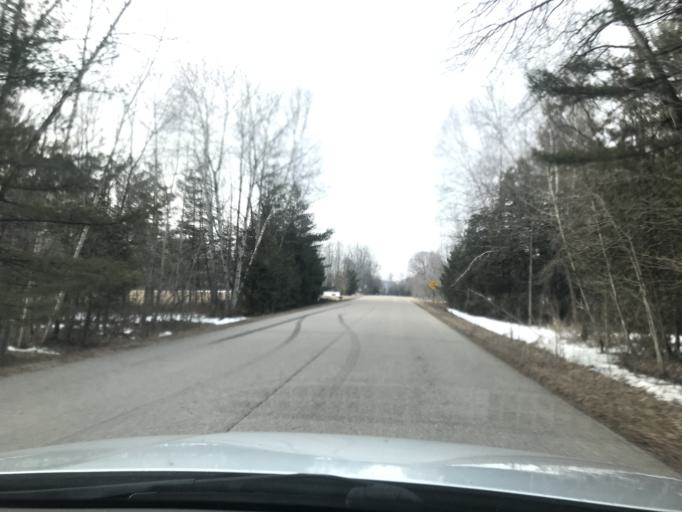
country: US
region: Wisconsin
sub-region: Oconto County
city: Oconto Falls
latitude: 44.8533
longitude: -88.1472
